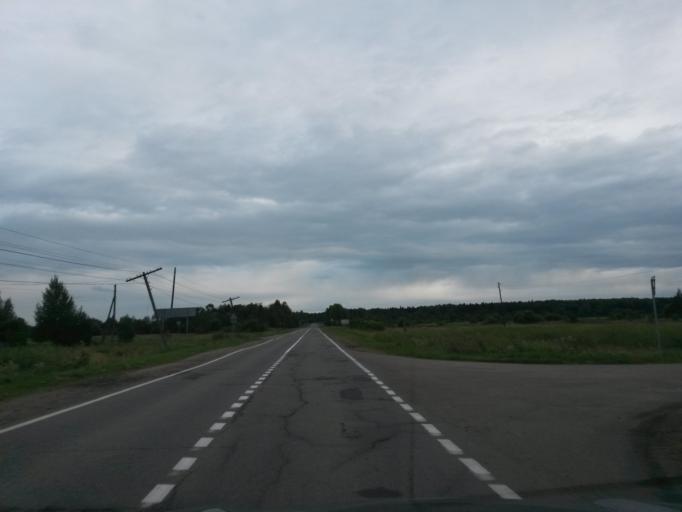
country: RU
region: Jaroslavl
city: Tutayev
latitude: 57.9347
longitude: 39.5014
